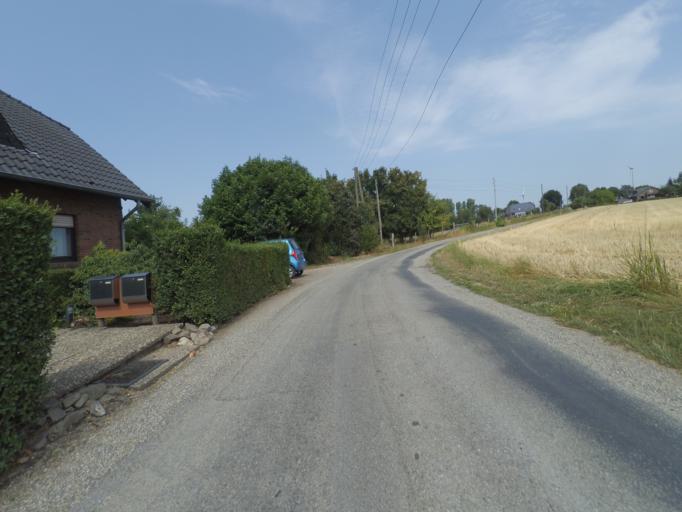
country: DE
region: North Rhine-Westphalia
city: Rees
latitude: 51.7807
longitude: 6.4385
